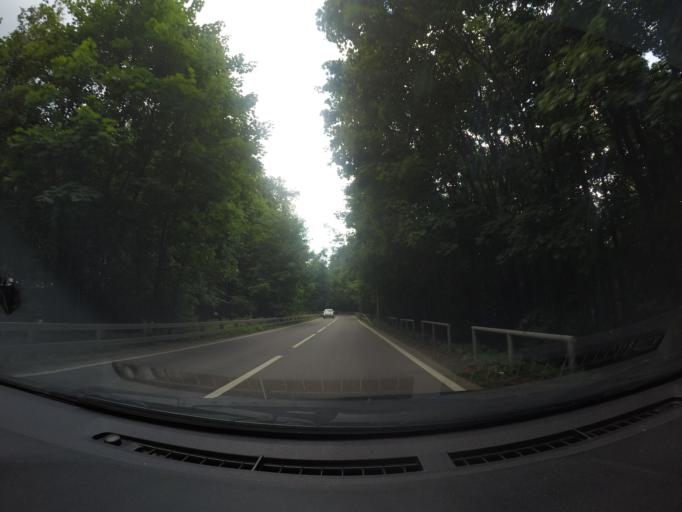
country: RU
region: Moscow
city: Sokol'niki
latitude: 55.8154
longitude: 37.6751
